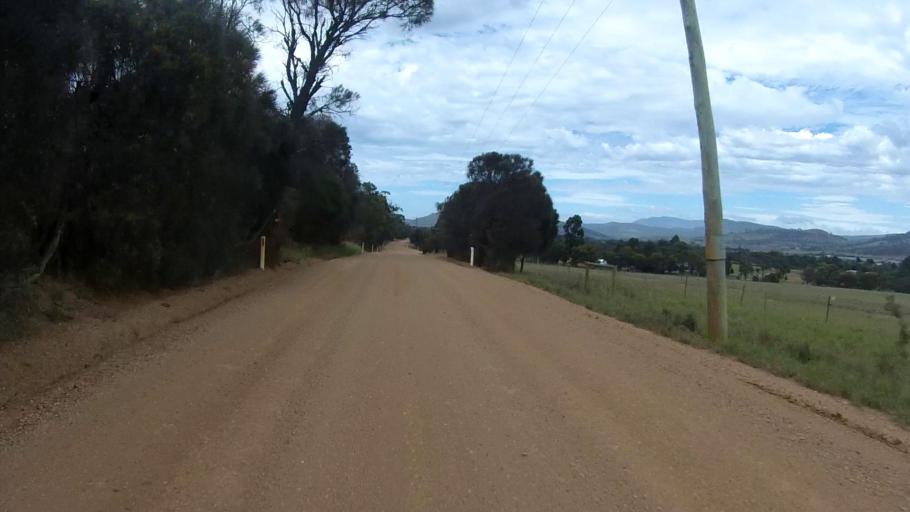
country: AU
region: Tasmania
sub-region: Clarence
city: Cambridge
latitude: -42.7044
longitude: 147.4572
